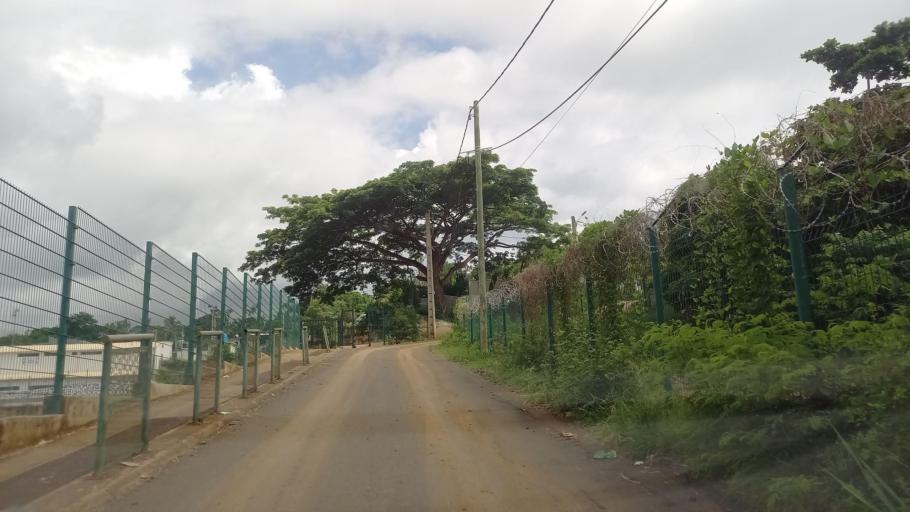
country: YT
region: Sada
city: Sada
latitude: -12.8487
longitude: 45.1061
